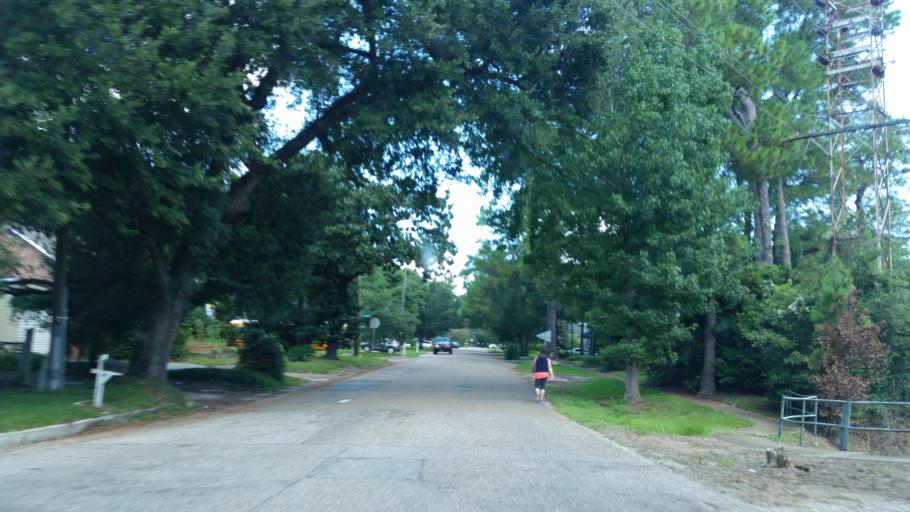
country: US
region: Alabama
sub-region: Mobile County
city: Mobile
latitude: 30.6785
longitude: -88.0913
